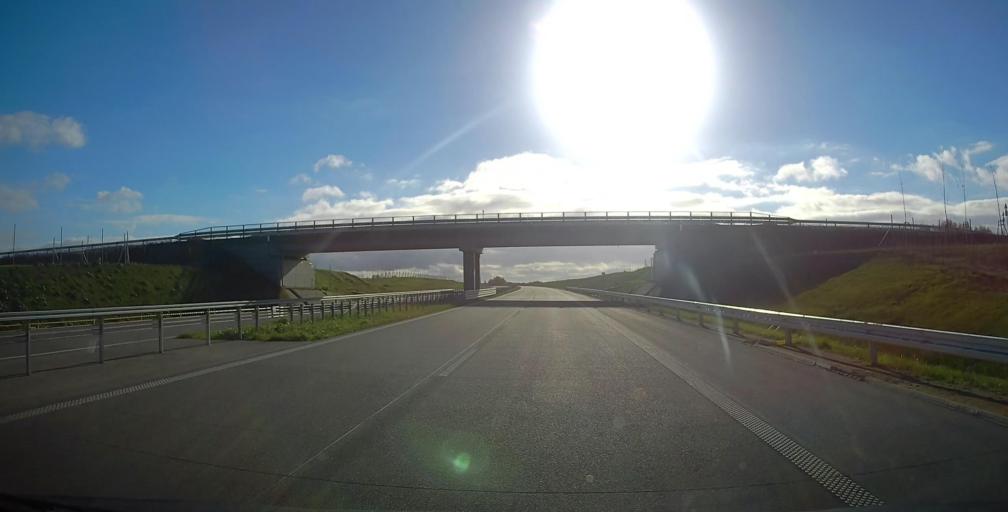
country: PL
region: Warmian-Masurian Voivodeship
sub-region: Powiat elcki
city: Elk
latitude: 53.7267
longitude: 22.2827
